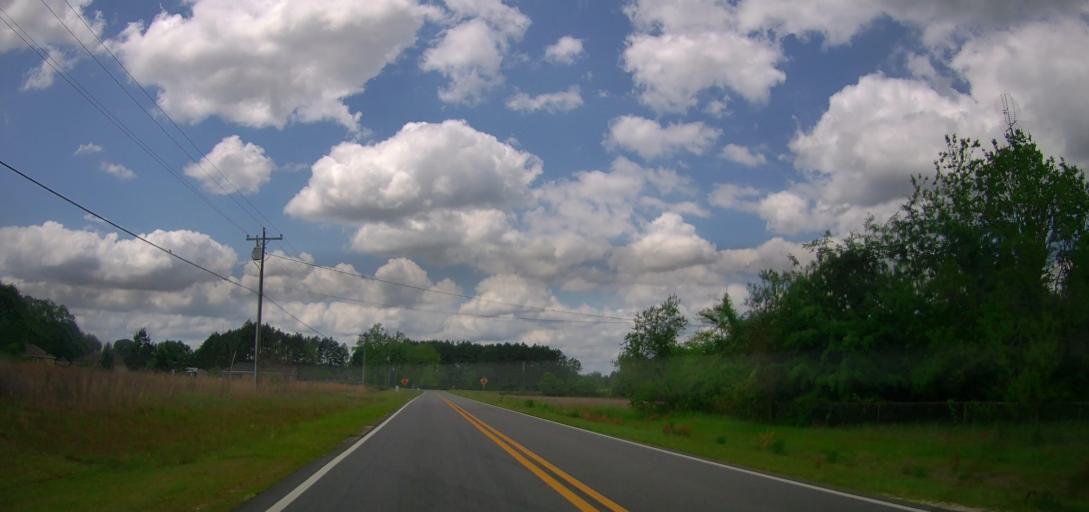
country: US
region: Georgia
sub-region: Laurens County
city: Dublin
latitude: 32.6004
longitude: -82.9536
